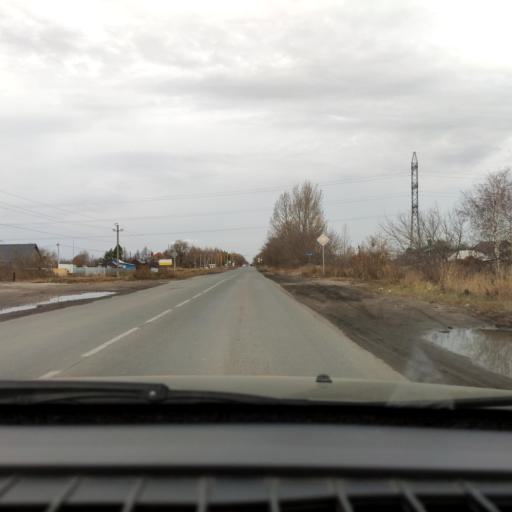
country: RU
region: Samara
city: Tol'yatti
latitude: 53.5750
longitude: 49.3321
